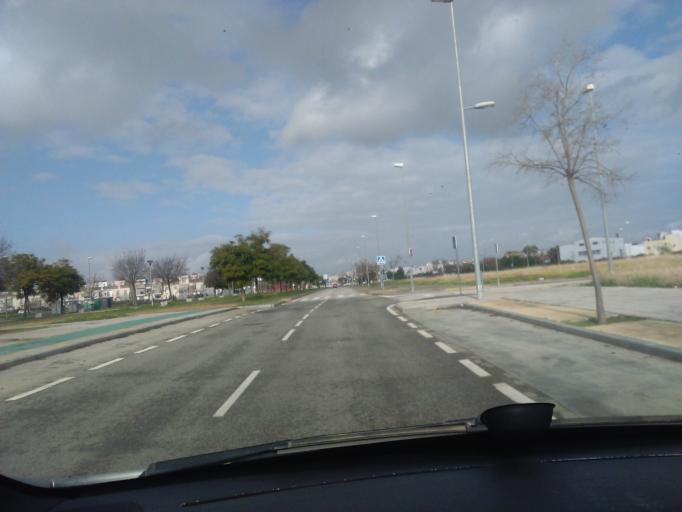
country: ES
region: Andalusia
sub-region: Provincia de Sevilla
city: Sevilla
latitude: 37.3796
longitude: -5.9143
